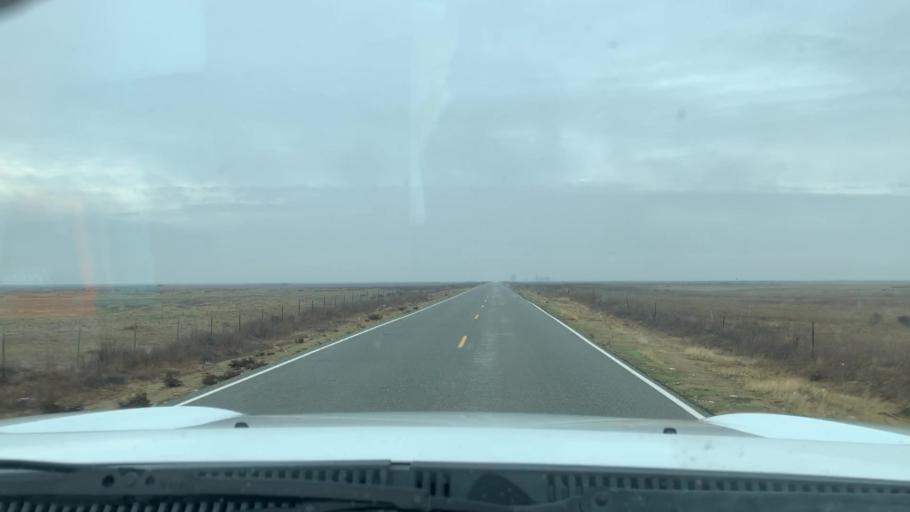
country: US
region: California
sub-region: Kern County
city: Lost Hills
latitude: 35.6467
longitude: -119.5801
